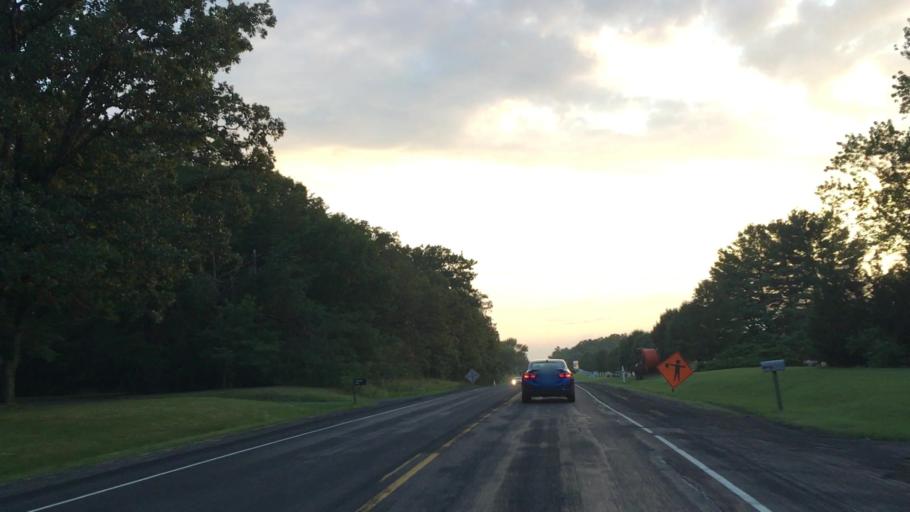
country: US
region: Virginia
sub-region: Spotsylvania County
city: Spotsylvania
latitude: 38.3063
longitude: -77.8046
